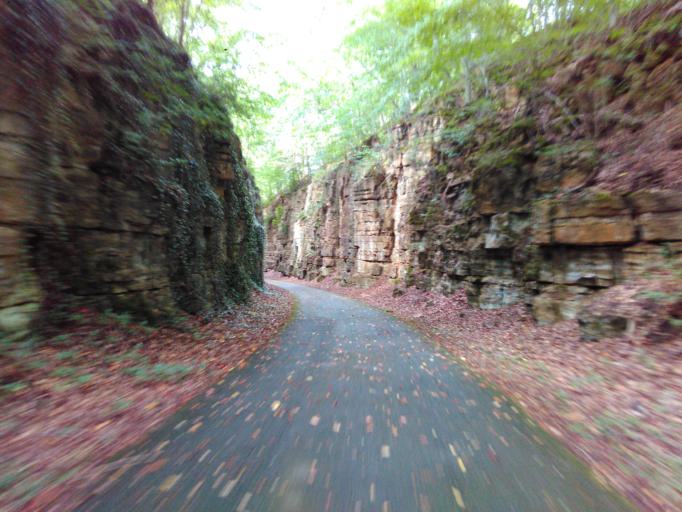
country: LU
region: Grevenmacher
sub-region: Canton d'Echternach
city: Berdorf
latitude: 49.7875
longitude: 6.3651
